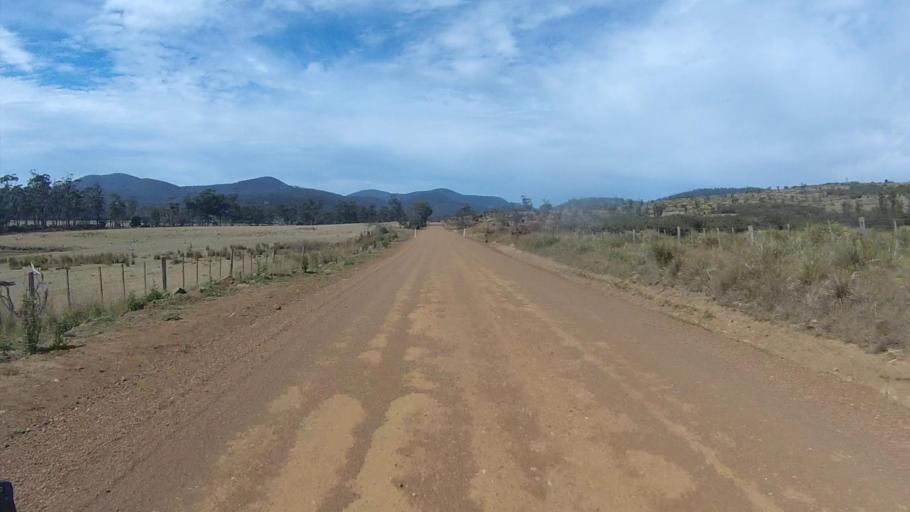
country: AU
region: Tasmania
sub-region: Sorell
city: Sorell
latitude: -42.6293
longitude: 147.9020
